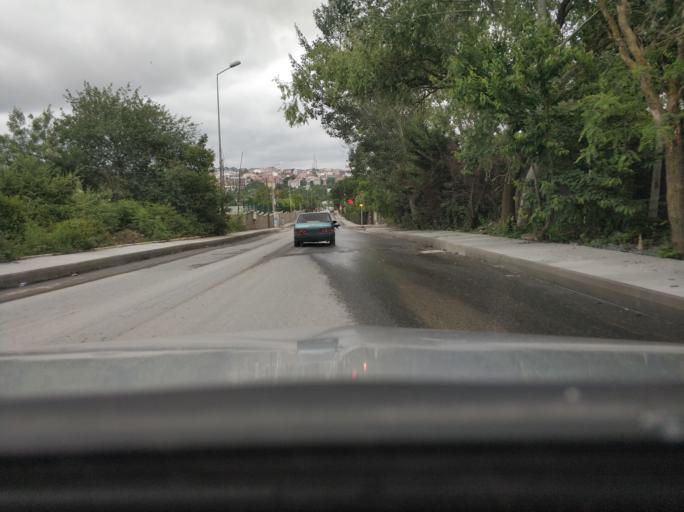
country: TR
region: Istanbul
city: Kemerburgaz
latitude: 41.1612
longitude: 28.8989
